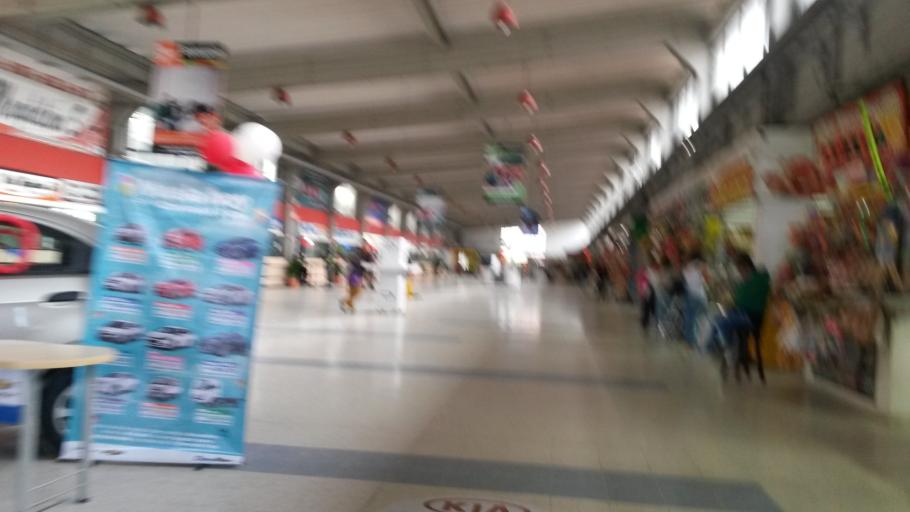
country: CO
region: Cauca
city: Popayan
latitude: 2.4508
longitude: -76.6084
